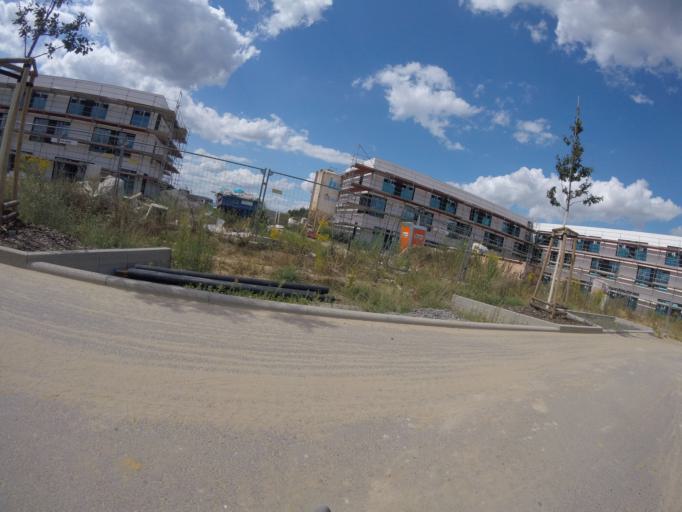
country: DE
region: Brandenburg
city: Werder
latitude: 52.4152
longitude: 12.9793
